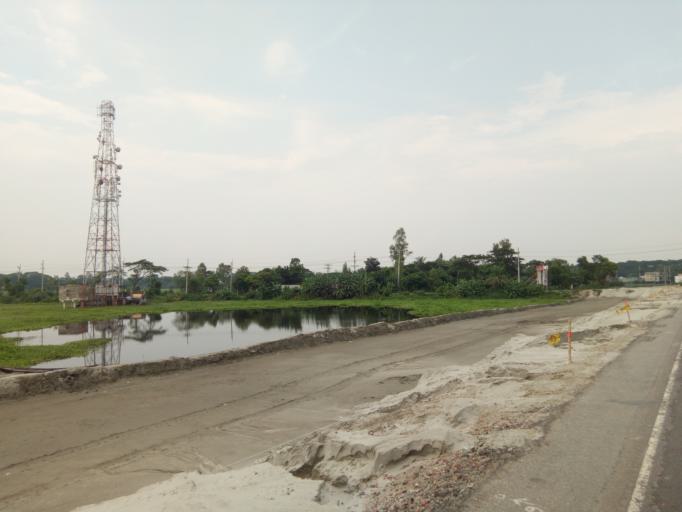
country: BD
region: Dhaka
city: Dohar
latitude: 23.5245
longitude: 90.2852
